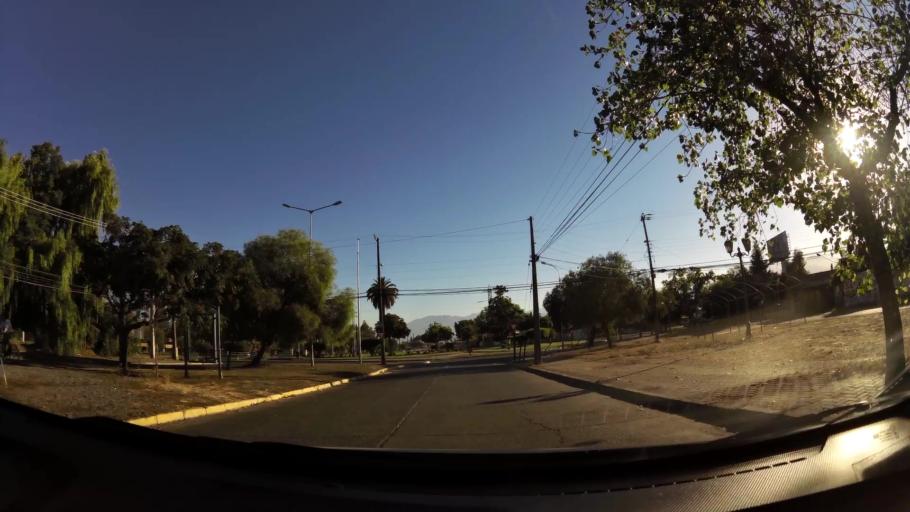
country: CL
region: O'Higgins
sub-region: Provincia de Cachapoal
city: Rancagua
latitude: -34.1693
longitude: -70.7185
